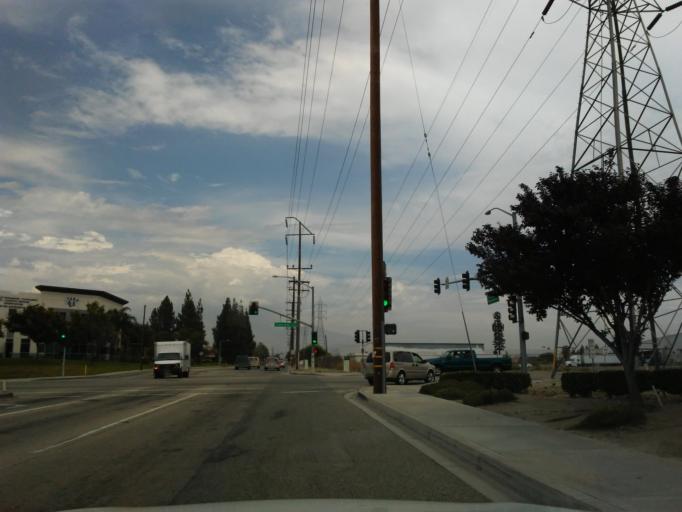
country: US
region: California
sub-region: San Bernardino County
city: Loma Linda
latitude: 34.0775
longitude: -117.2602
